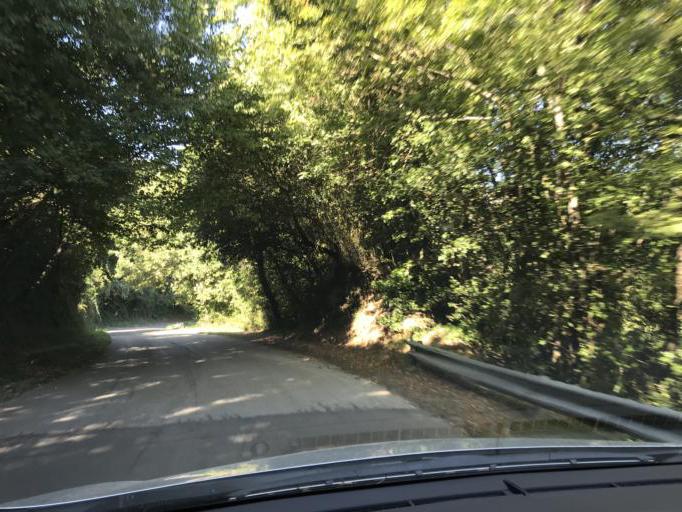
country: IT
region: Umbria
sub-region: Provincia di Terni
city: Avigliano Umbro
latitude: 42.6168
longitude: 12.4091
